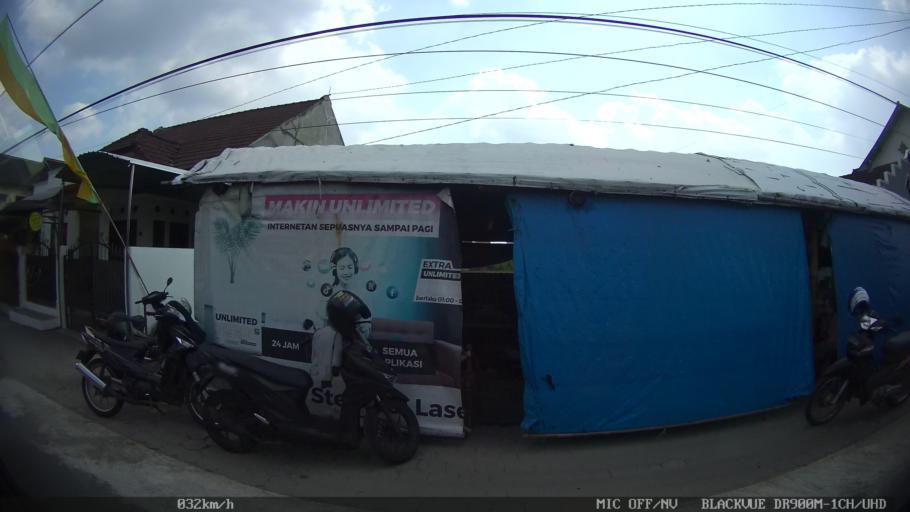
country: ID
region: Daerah Istimewa Yogyakarta
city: Yogyakarta
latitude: -7.8046
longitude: 110.4053
